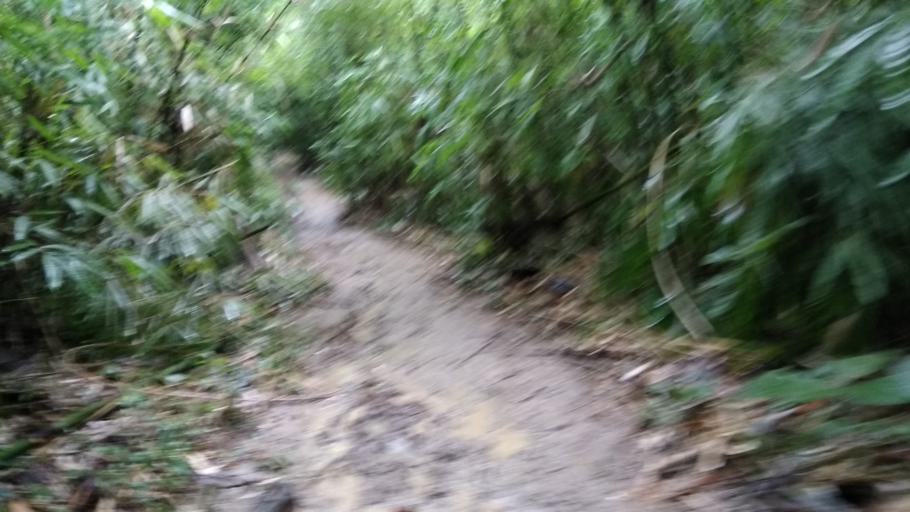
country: IN
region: Tripura
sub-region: Dhalai
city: Kamalpur
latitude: 24.1694
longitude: 91.9004
